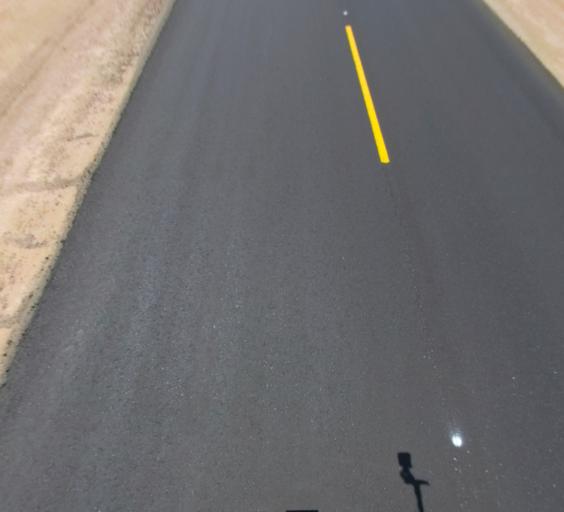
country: US
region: California
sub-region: Madera County
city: Bonadelle Ranchos-Madera Ranchos
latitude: 36.8902
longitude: -119.8574
